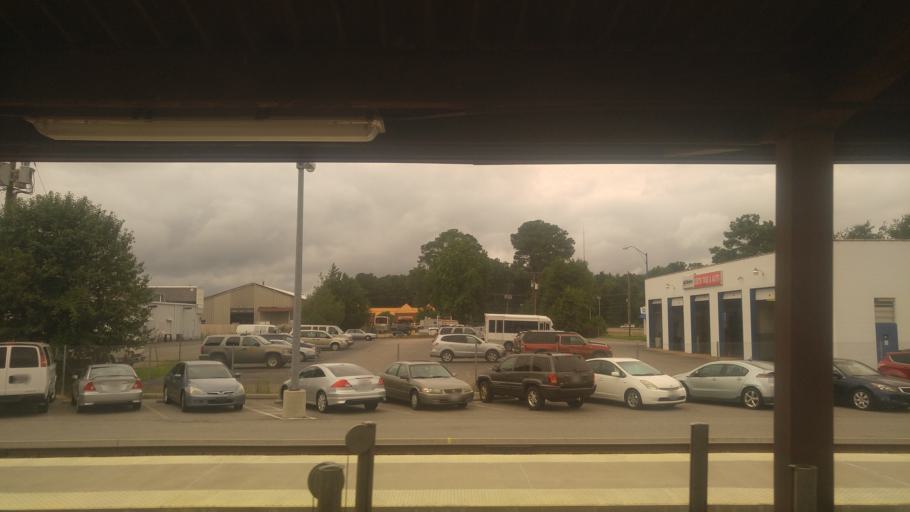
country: US
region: Virginia
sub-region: Henrico County
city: Dumbarton
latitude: 37.6168
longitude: -77.4960
